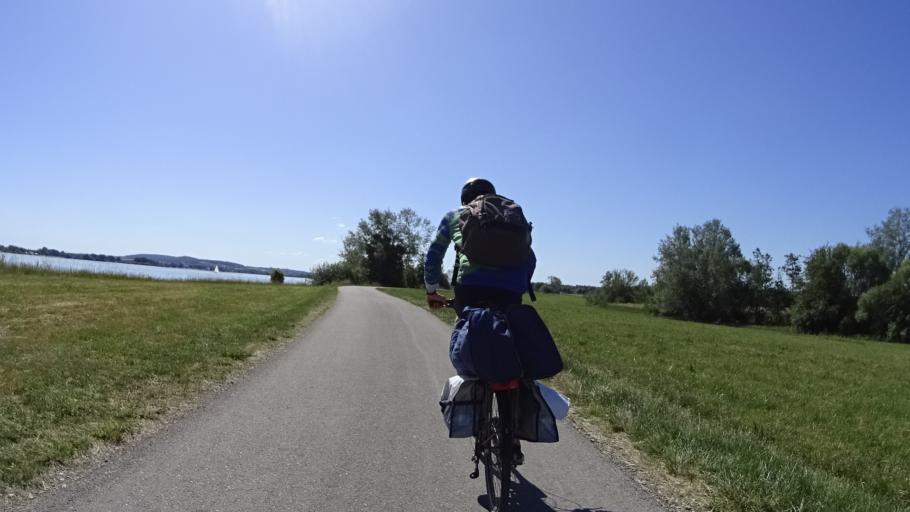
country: DE
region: Bavaria
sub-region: Regierungsbezirk Mittelfranken
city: Muhr am See
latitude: 49.1319
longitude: 10.7148
